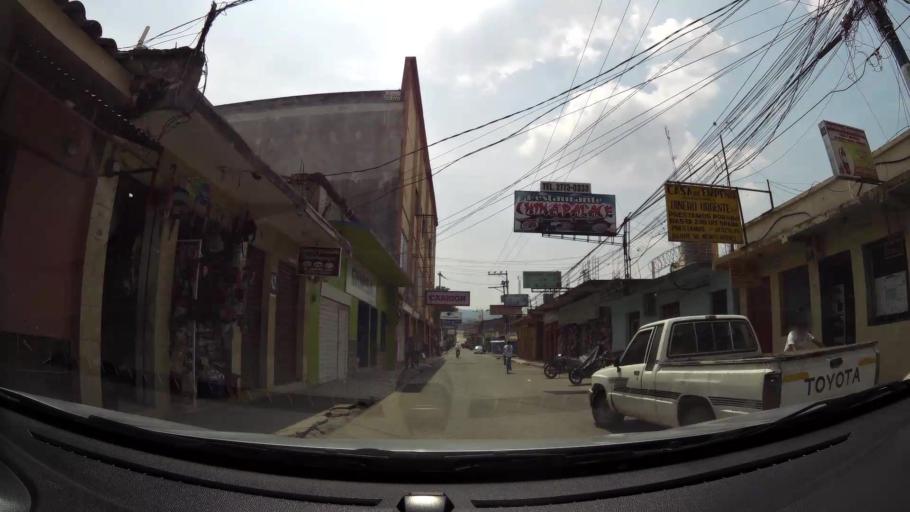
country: HN
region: Comayagua
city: Siguatepeque
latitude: 14.5964
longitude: -87.8305
